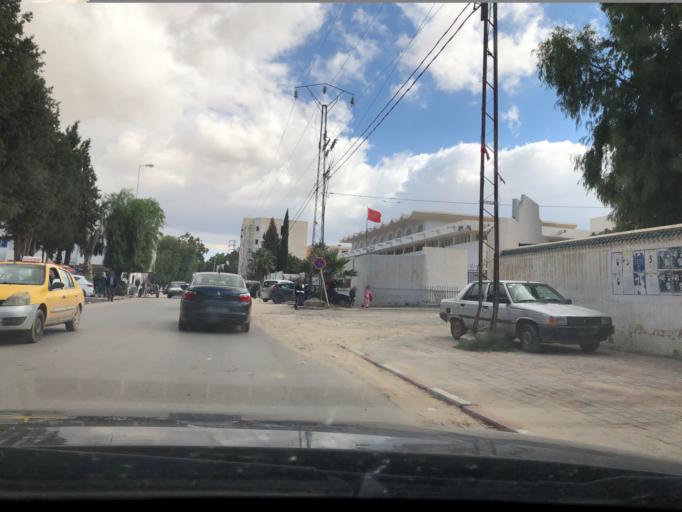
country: TN
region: Al Qasrayn
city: Kasserine
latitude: 35.1665
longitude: 8.8256
